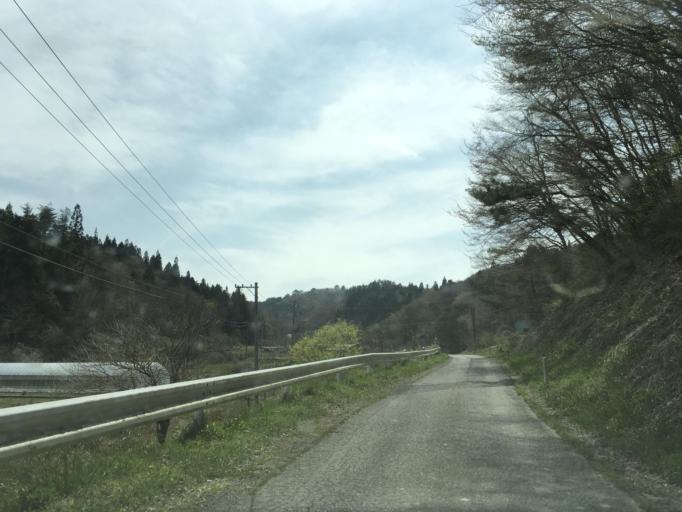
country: JP
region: Iwate
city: Ichinoseki
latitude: 38.8258
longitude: 141.3495
